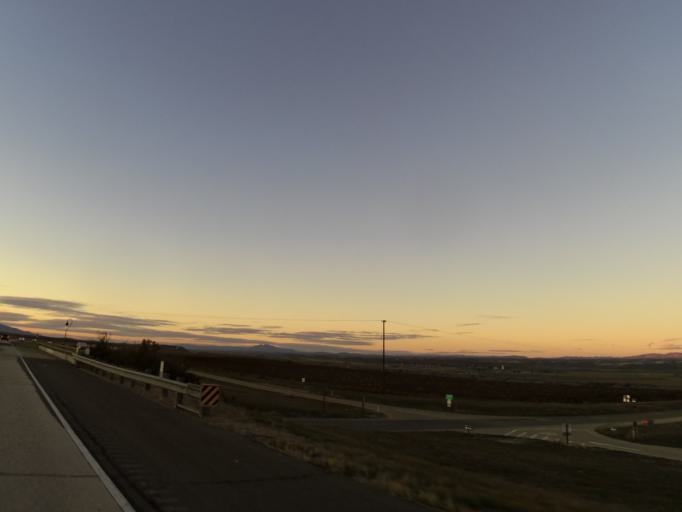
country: US
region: California
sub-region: Monterey County
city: King City
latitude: 36.0937
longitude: -121.0207
